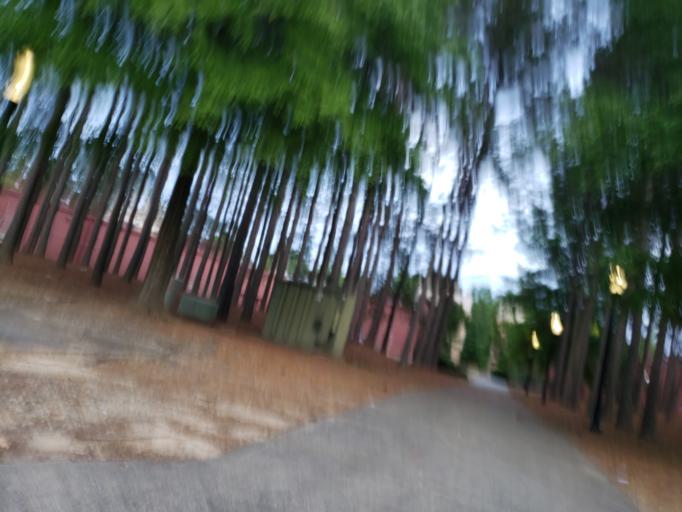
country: US
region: North Carolina
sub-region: Durham County
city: Durham
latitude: 35.9134
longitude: -78.9363
